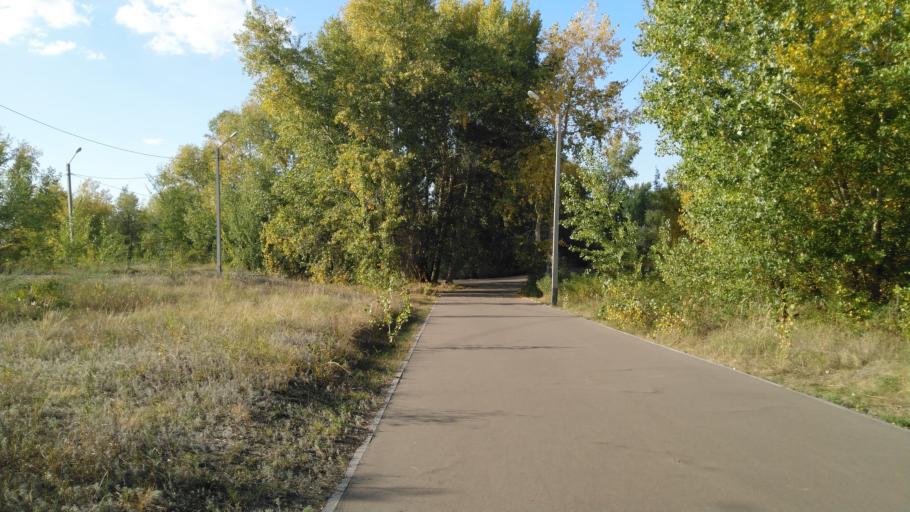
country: KZ
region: Pavlodar
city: Pavlodar
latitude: 52.2623
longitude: 76.9315
